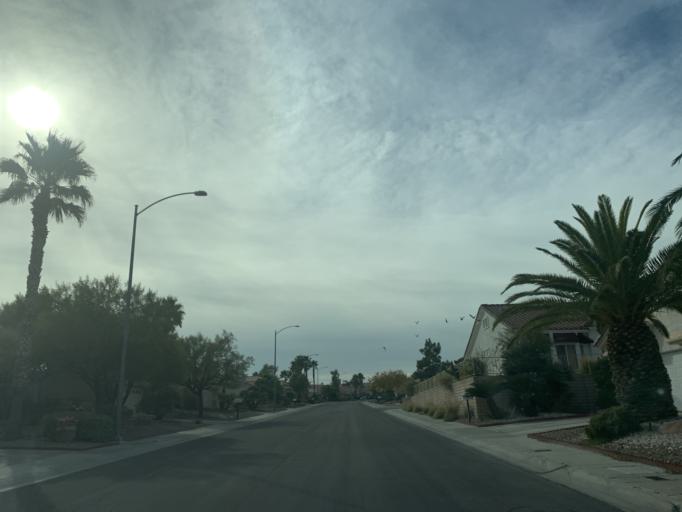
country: US
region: Nevada
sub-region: Clark County
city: Summerlin South
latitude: 36.2170
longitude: -115.3236
